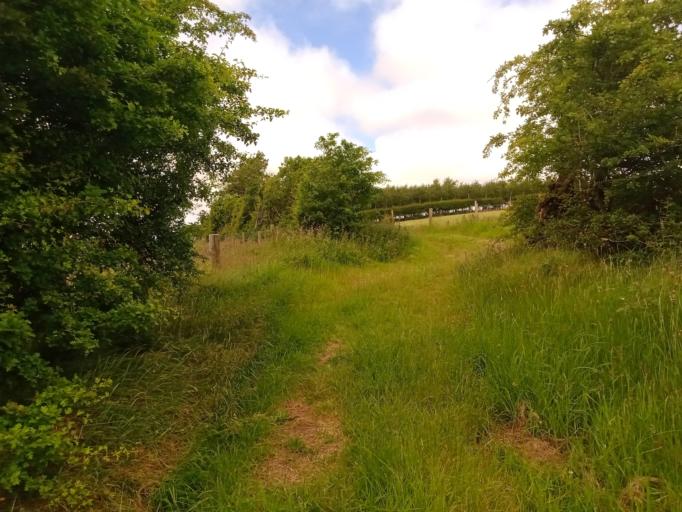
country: IE
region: Leinster
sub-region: Kilkenny
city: Ballyragget
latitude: 52.7923
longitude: -7.4553
